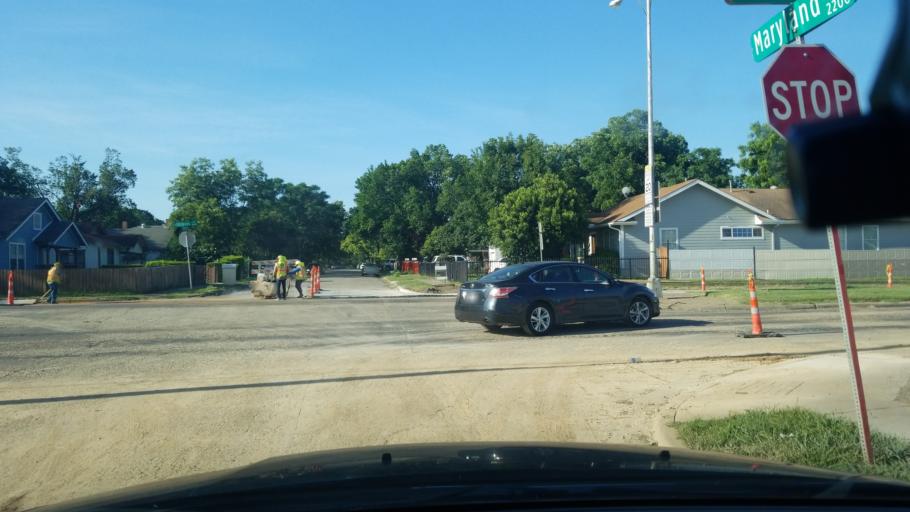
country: US
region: Texas
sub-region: Dallas County
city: Dallas
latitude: 32.7205
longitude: -96.8133
